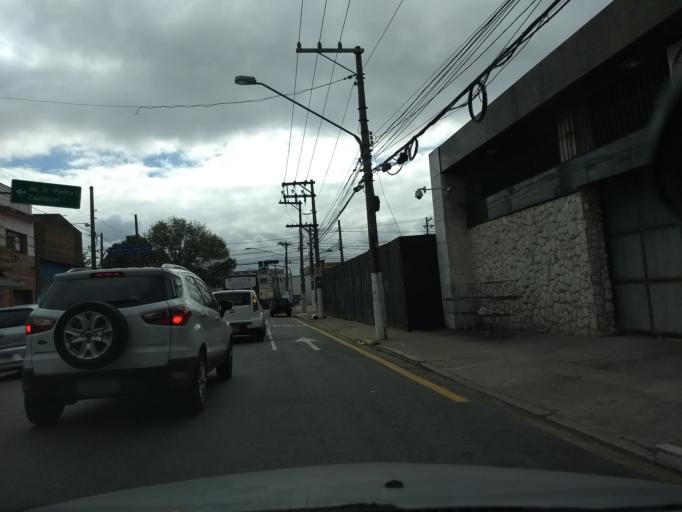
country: BR
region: Sao Paulo
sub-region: Sao Paulo
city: Sao Paulo
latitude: -23.5778
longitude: -46.6086
